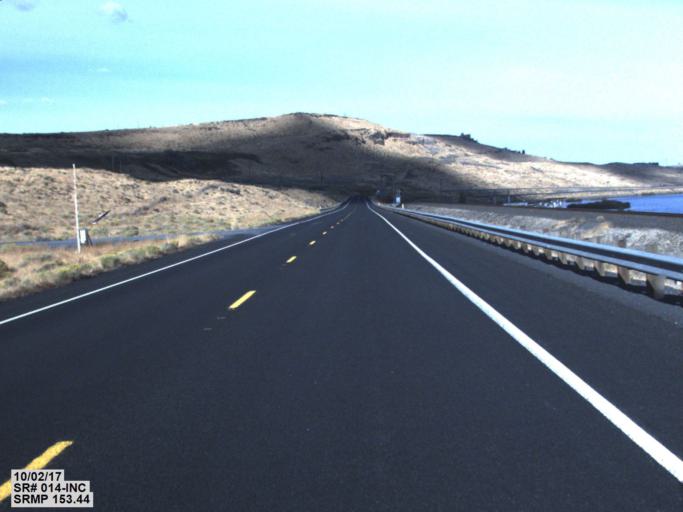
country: US
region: Oregon
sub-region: Morrow County
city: Boardman
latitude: 45.8620
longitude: -119.8558
